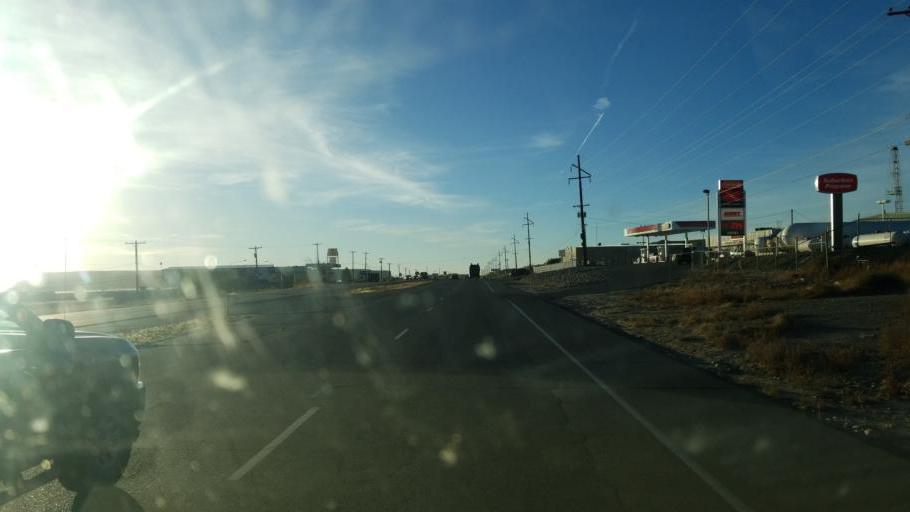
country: US
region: New Mexico
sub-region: San Juan County
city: Lee Acres
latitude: 36.7038
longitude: -108.1030
